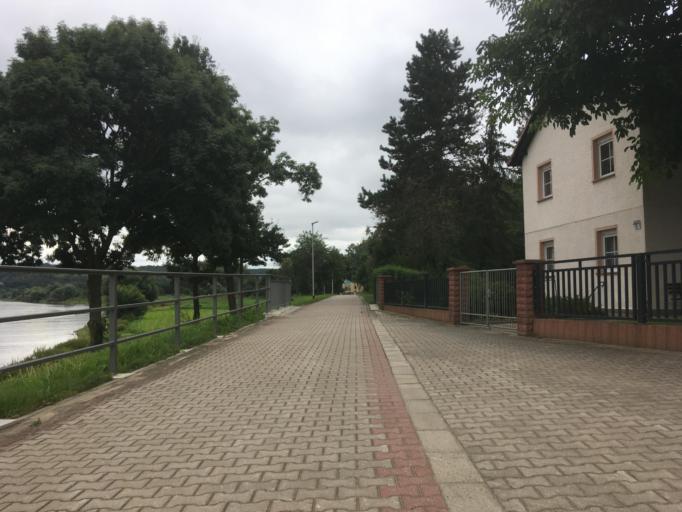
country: DE
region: Saxony
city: Weissig
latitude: 51.2387
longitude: 13.4111
